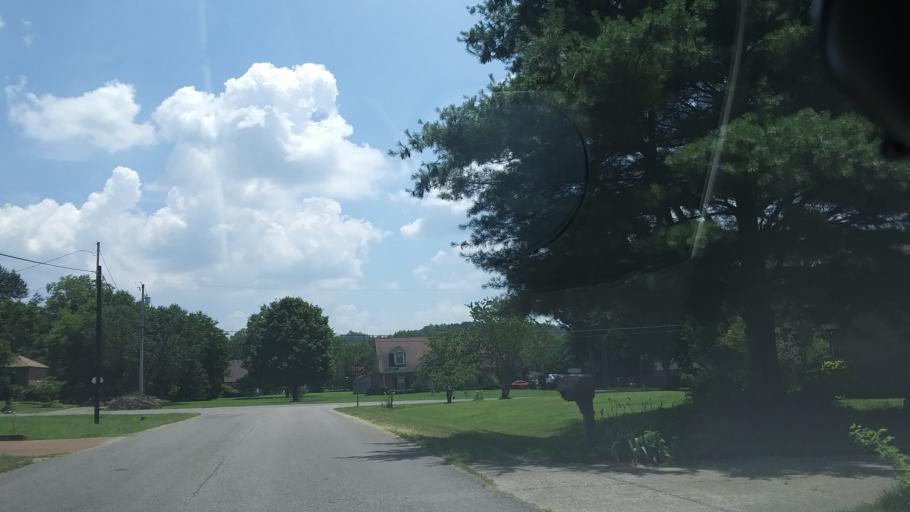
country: US
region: Tennessee
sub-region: Davidson County
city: Belle Meade
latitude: 36.0875
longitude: -86.9489
